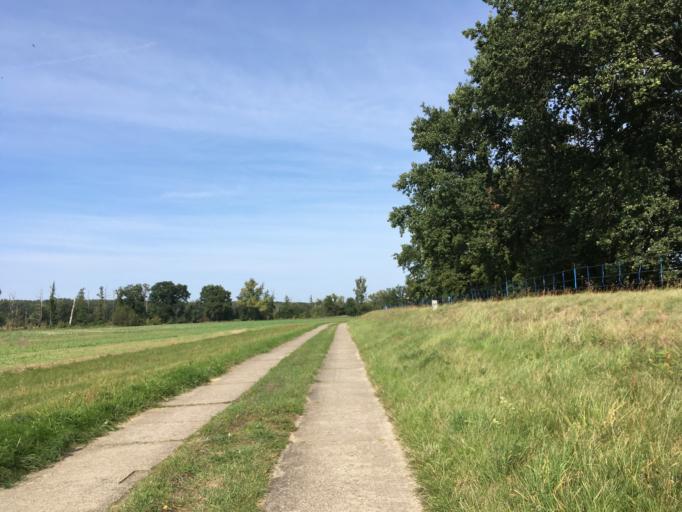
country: DE
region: Brandenburg
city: Guben
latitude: 52.0029
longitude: 14.7133
